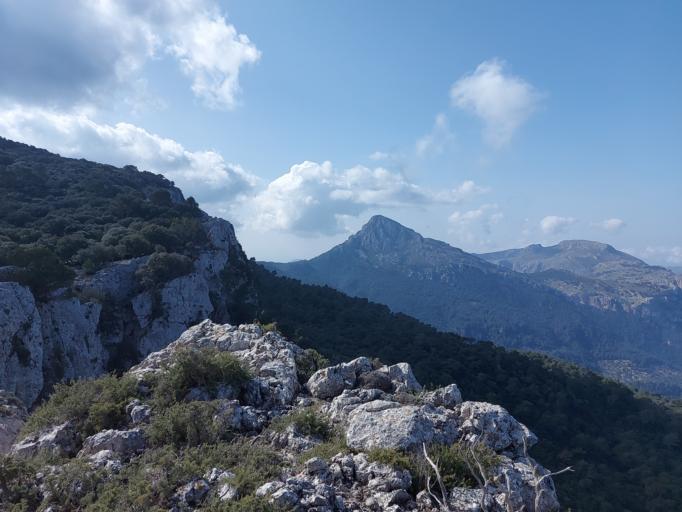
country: ES
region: Balearic Islands
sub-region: Illes Balears
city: Estellencs
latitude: 39.6595
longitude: 2.5084
